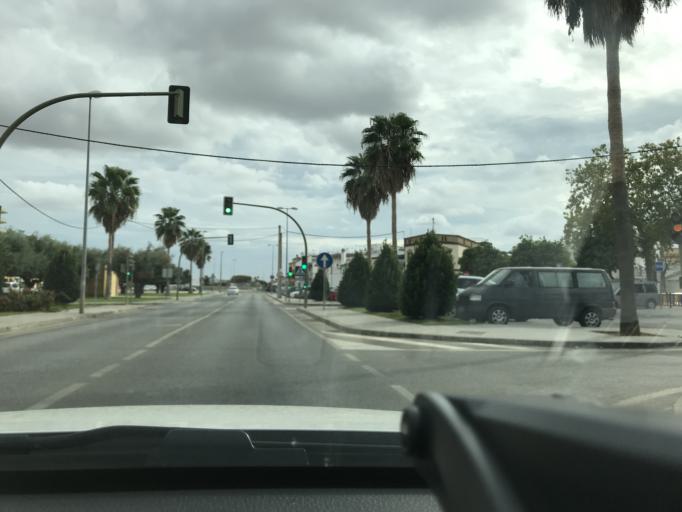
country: ES
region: Andalusia
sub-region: Provincia de Sevilla
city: La Rinconada
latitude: 37.4881
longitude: -5.9779
